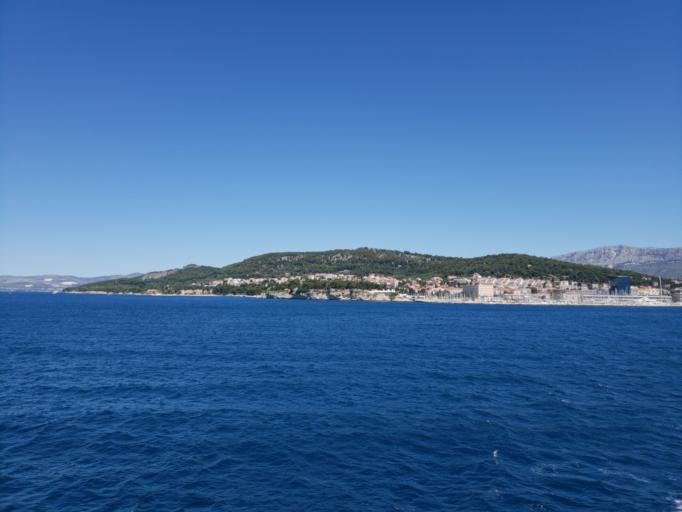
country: HR
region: Splitsko-Dalmatinska
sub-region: Grad Split
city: Split
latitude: 43.4951
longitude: 16.4339
